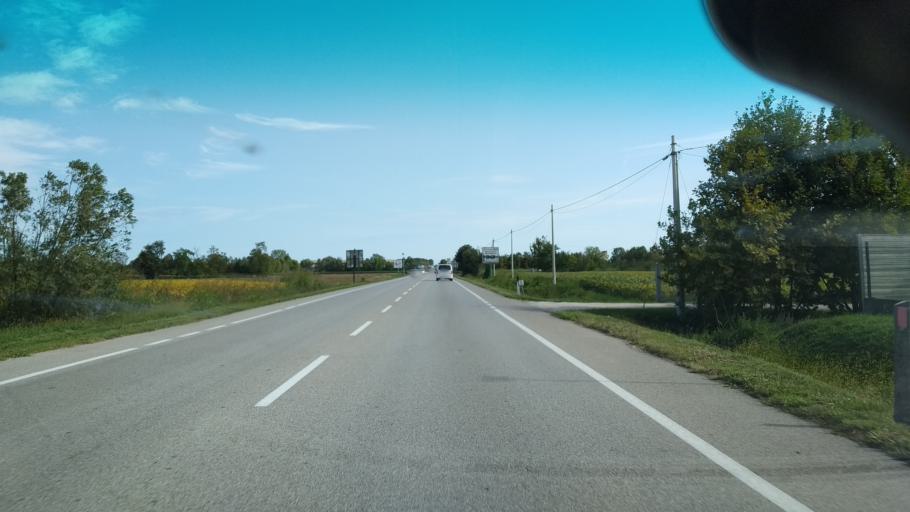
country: IT
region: Veneto
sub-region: Provincia di Padova
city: Corte
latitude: 45.2892
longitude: 12.0665
